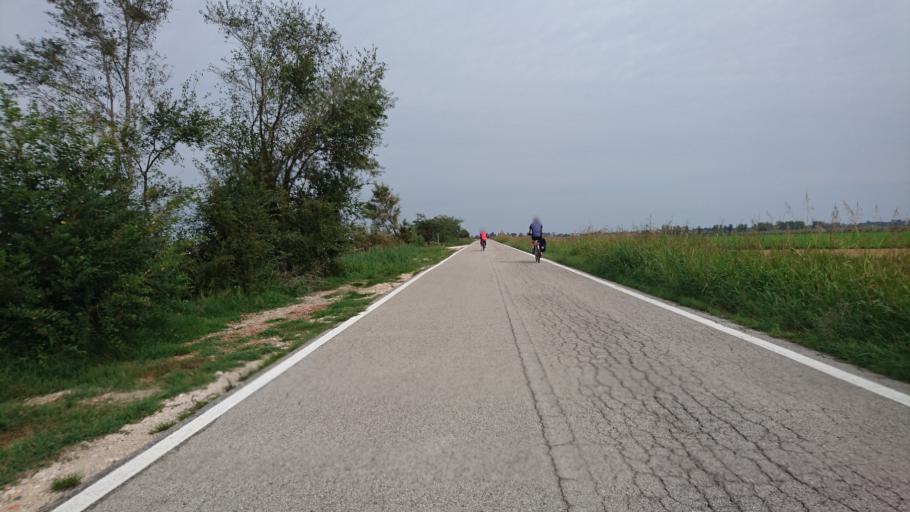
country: IT
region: Veneto
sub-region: Provincia di Rovigo
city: Scardovari
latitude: 44.8623
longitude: 12.4412
